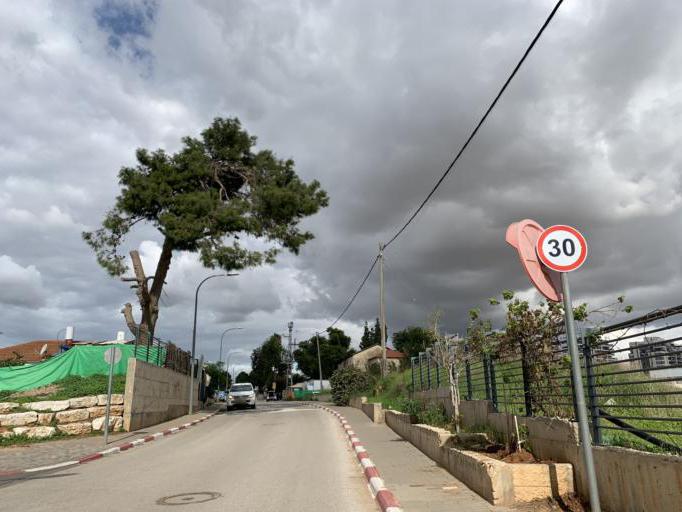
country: IL
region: Central District
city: Hod HaSharon
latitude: 32.1615
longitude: 34.8961
